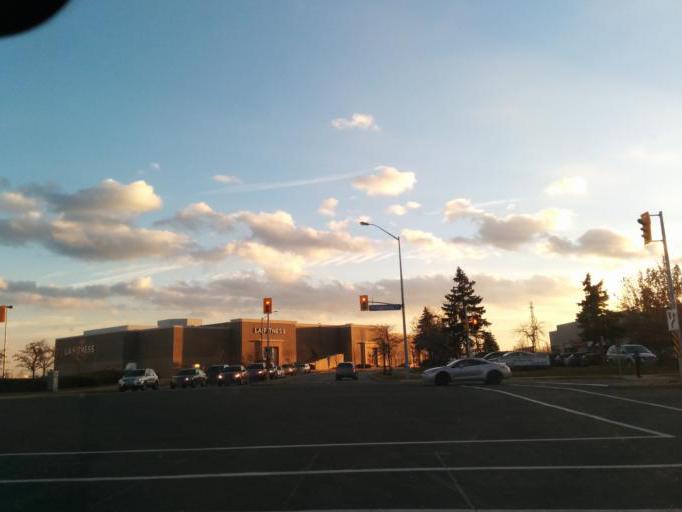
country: CA
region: Ontario
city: Mississauga
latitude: 43.5187
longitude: -79.6907
